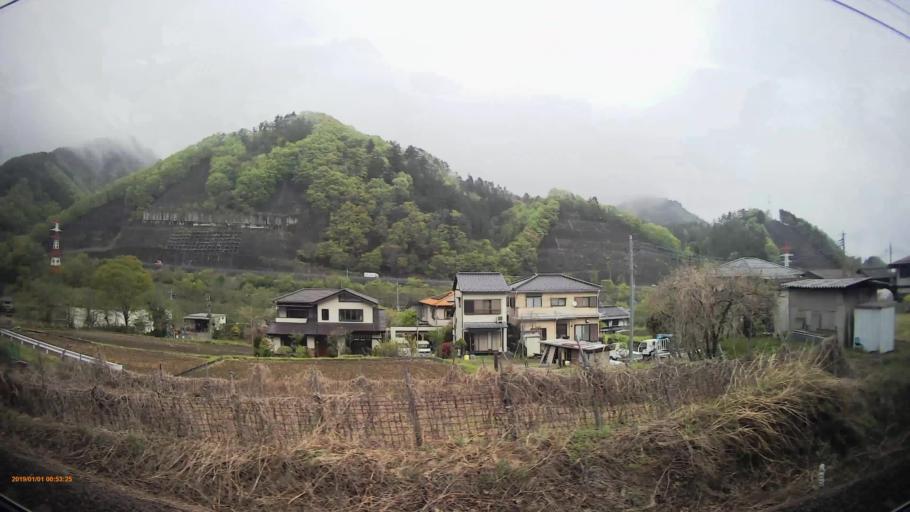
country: JP
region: Yamanashi
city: Otsuki
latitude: 35.5982
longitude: 138.8694
